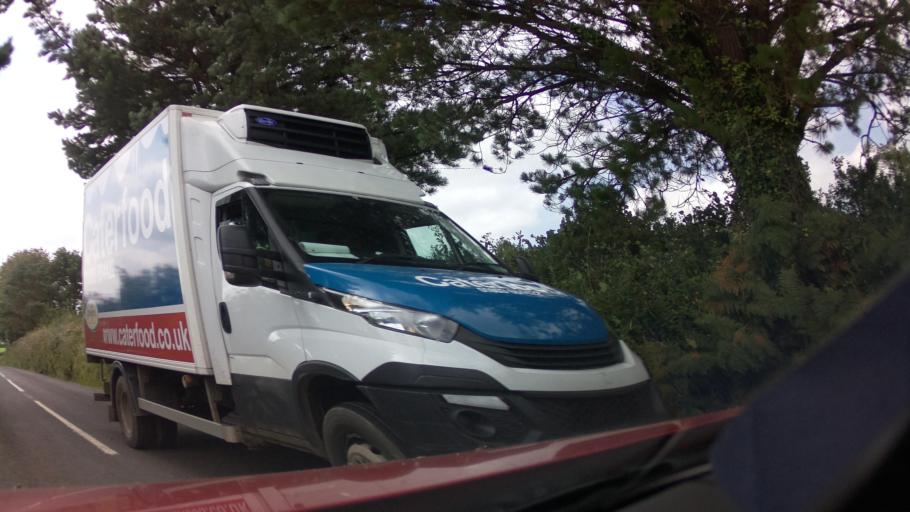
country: GB
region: England
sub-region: Devon
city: South Brent
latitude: 50.3936
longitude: -3.8412
